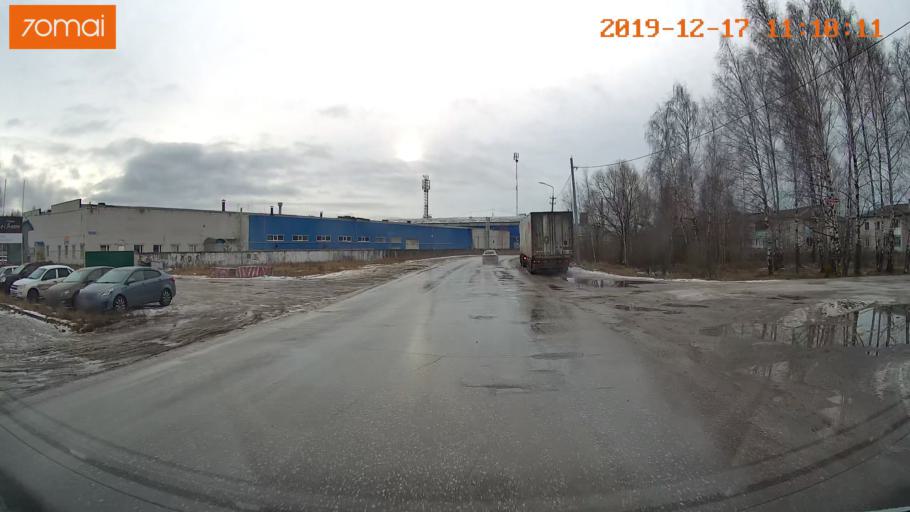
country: RU
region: Vladimir
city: Gus'-Khrustal'nyy
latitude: 55.5947
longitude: 40.6422
